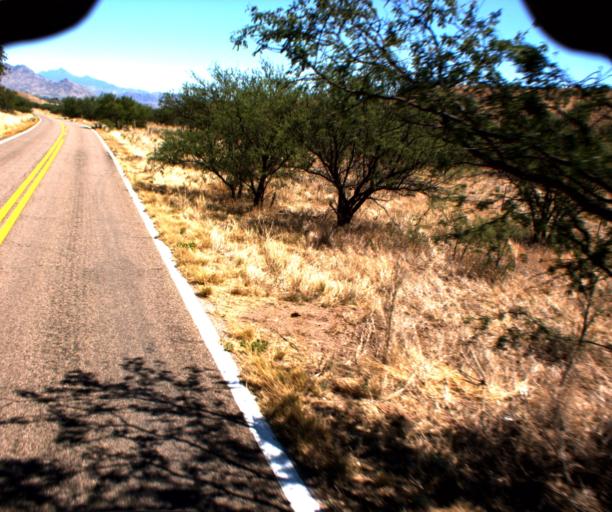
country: US
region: Arizona
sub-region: Santa Cruz County
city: Rio Rico
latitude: 31.4046
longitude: -111.0257
